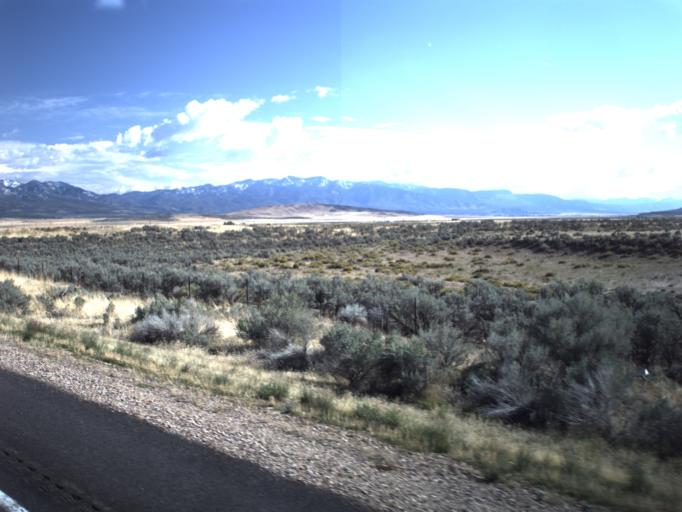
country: US
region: Utah
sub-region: Millard County
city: Fillmore
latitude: 39.1366
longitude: -112.3661
